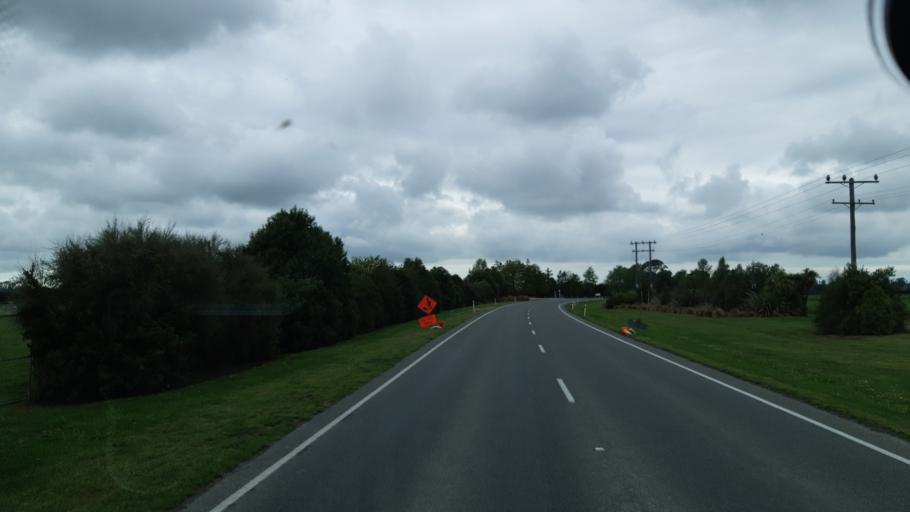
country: NZ
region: Canterbury
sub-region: Timaru District
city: Pleasant Point
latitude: -44.2686
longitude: 171.1551
